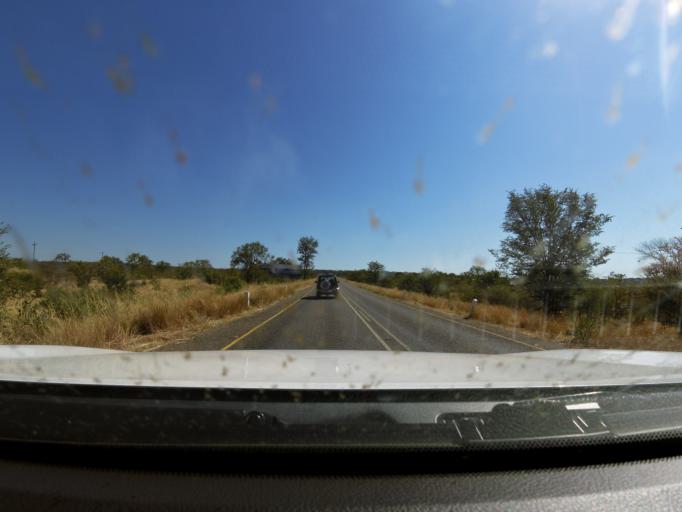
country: ZW
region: Matabeleland North
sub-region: Hwange District
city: Victoria Falls
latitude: -17.9649
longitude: 25.8220
